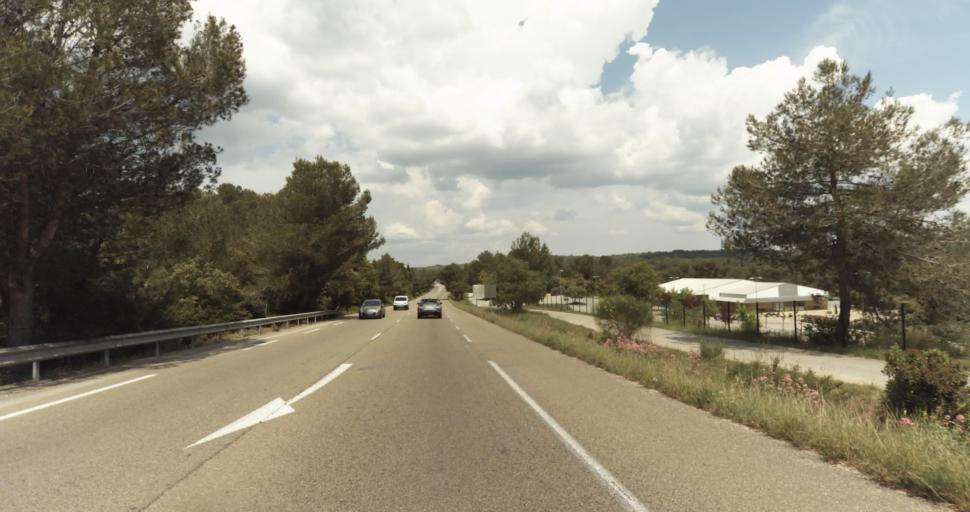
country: FR
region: Languedoc-Roussillon
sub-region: Departement du Gard
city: Nimes
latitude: 43.8633
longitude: 4.3234
